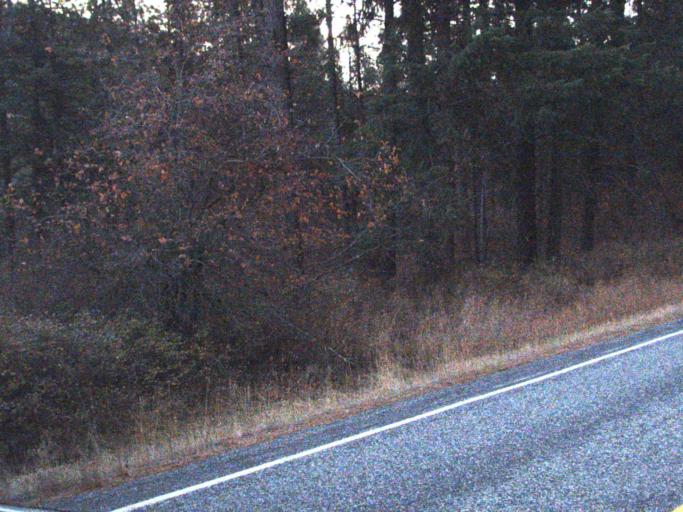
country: US
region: Washington
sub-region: Ferry County
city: Republic
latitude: 48.2979
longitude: -118.7344
